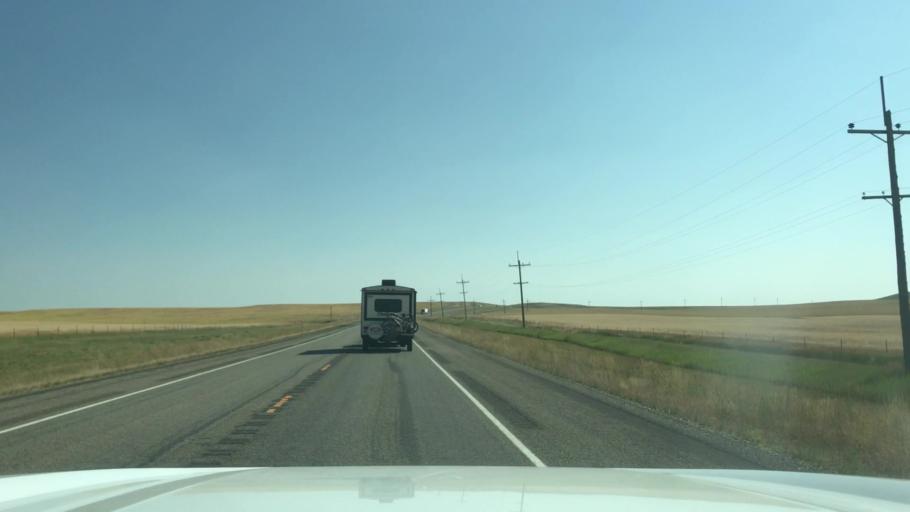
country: US
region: Montana
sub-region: Wheatland County
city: Harlowton
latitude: 46.4782
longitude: -109.7661
